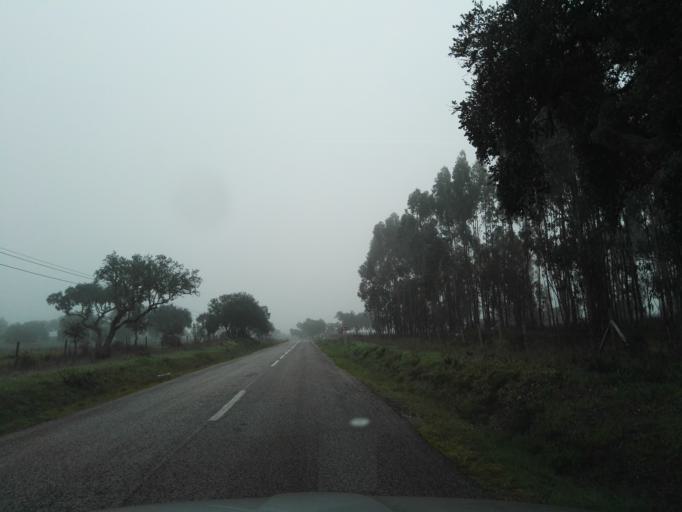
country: PT
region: Evora
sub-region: Montemor-O-Novo
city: Montemor-o-Novo
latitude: 38.7794
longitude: -8.2142
